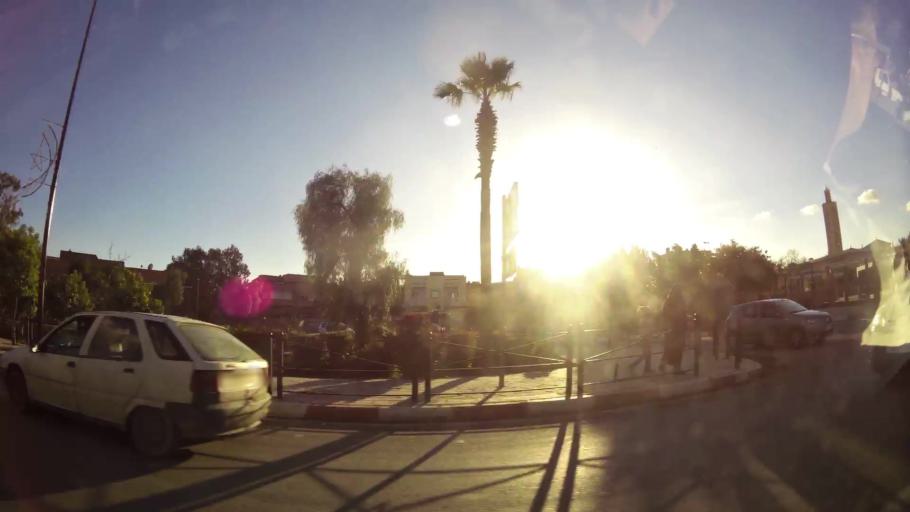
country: MA
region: Marrakech-Tensift-Al Haouz
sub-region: Kelaa-Des-Sraghna
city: Sidi Abdallah
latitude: 32.2348
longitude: -7.9583
